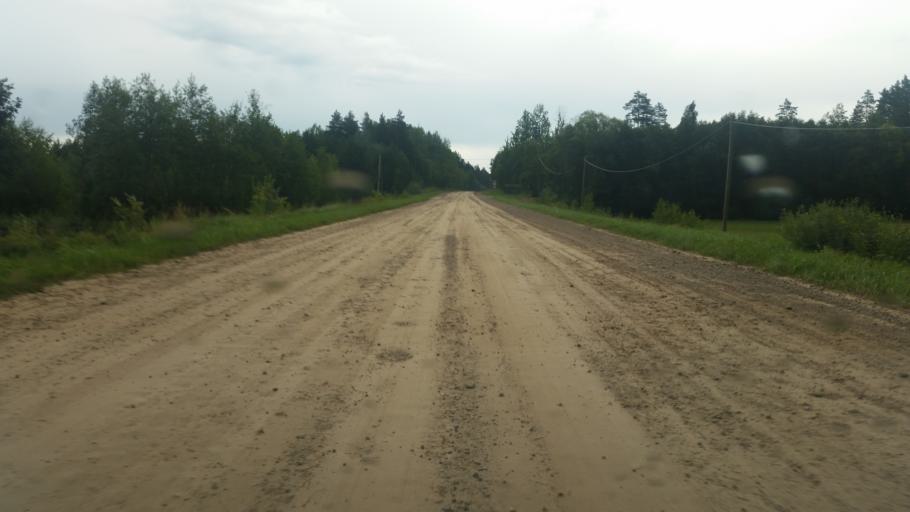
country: LV
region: Vecumnieki
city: Vecumnieki
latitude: 56.4441
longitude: 24.5769
